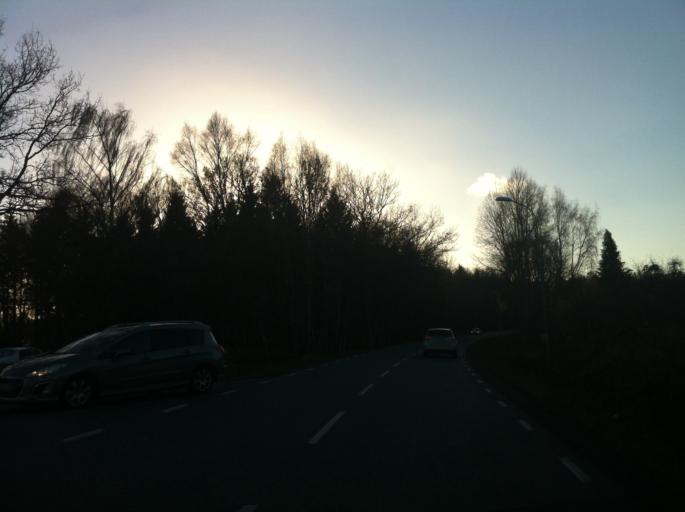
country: SE
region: Skane
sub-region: Ostra Goinge Kommun
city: Knislinge
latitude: 56.1970
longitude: 14.1008
